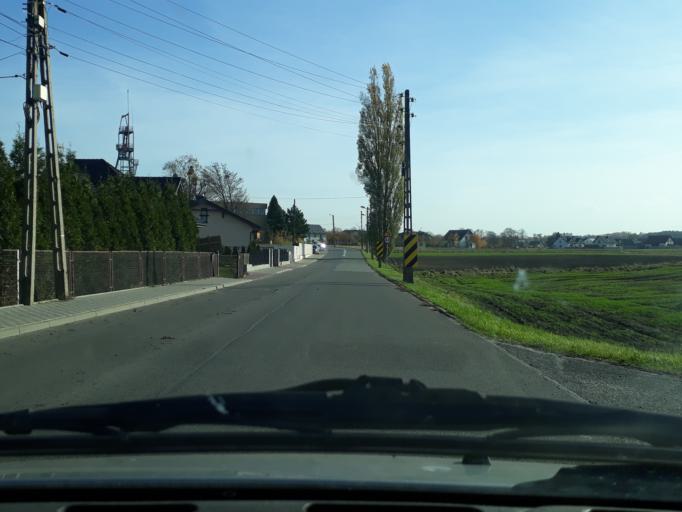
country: PL
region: Silesian Voivodeship
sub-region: Powiat tarnogorski
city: Tarnowskie Gory
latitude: 50.4263
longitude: 18.8473
